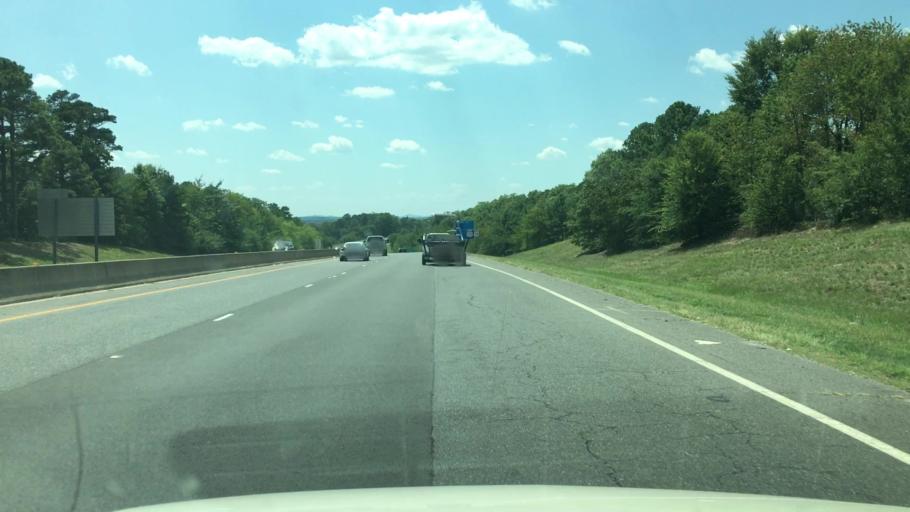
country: US
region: Arkansas
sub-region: Garland County
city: Hot Springs
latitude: 34.4660
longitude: -93.0773
